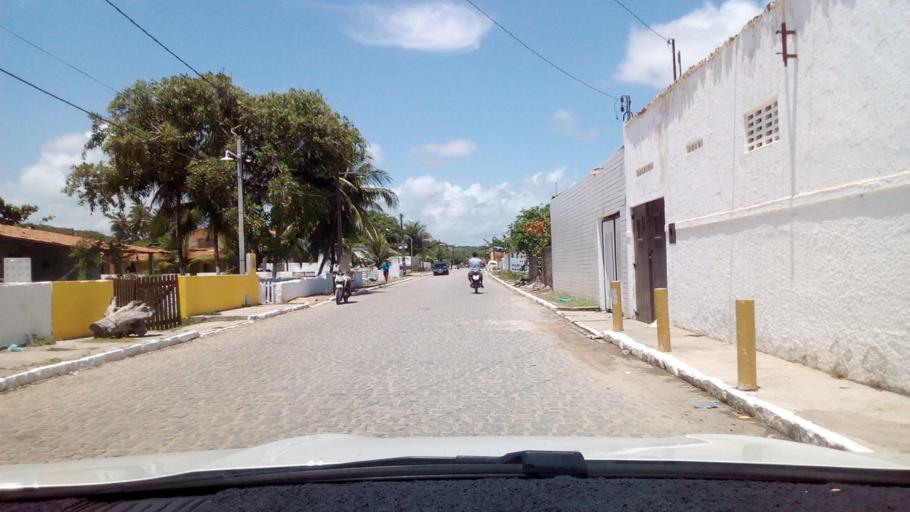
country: BR
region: Paraiba
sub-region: Pitimbu
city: Pitimbu
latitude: -7.5039
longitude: -34.8121
